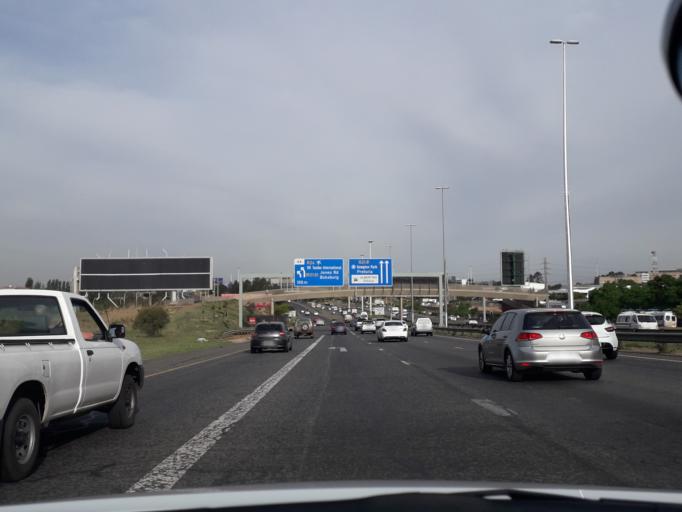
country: ZA
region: Gauteng
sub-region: City of Johannesburg Metropolitan Municipality
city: Modderfontein
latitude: -26.1297
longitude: 28.2156
